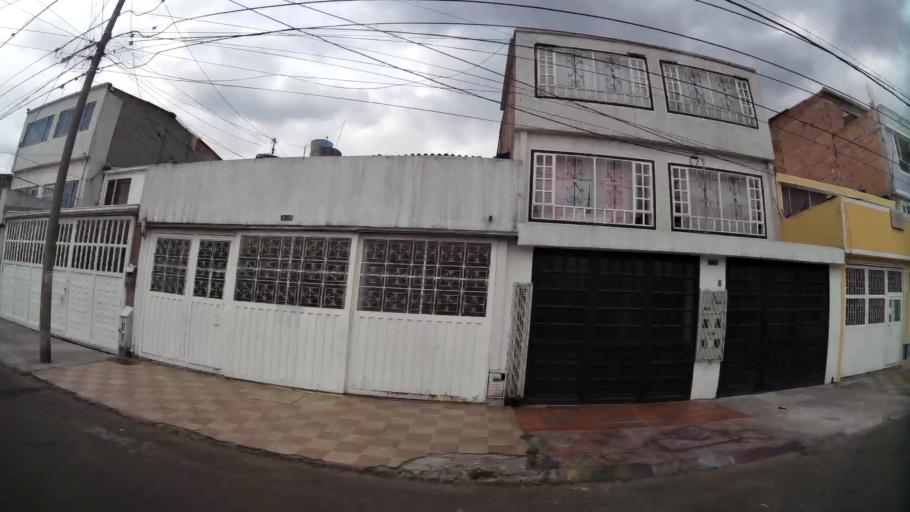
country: CO
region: Bogota D.C.
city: Bogota
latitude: 4.6207
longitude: -74.1147
